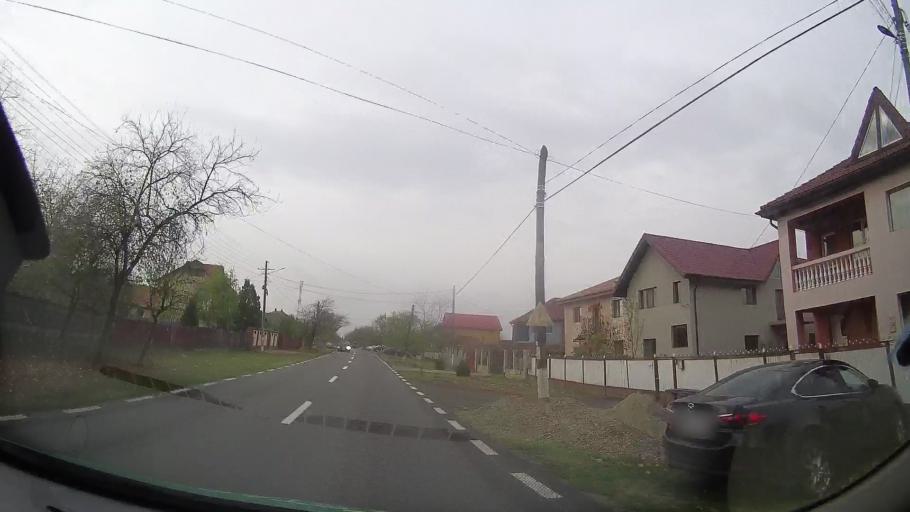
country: RO
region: Ilfov
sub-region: Comuna Gruiu
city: Lipia
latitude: 44.7147
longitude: 26.2559
